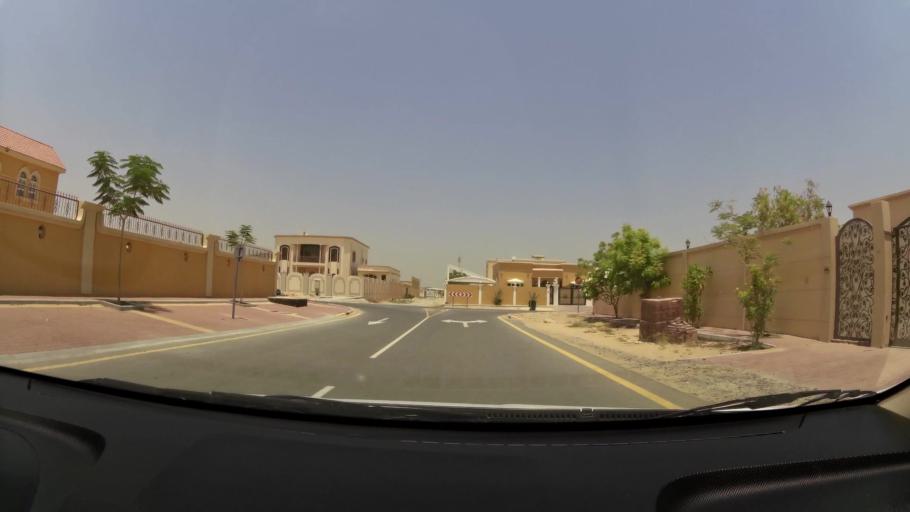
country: AE
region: Ajman
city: Ajman
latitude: 25.4092
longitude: 55.5293
